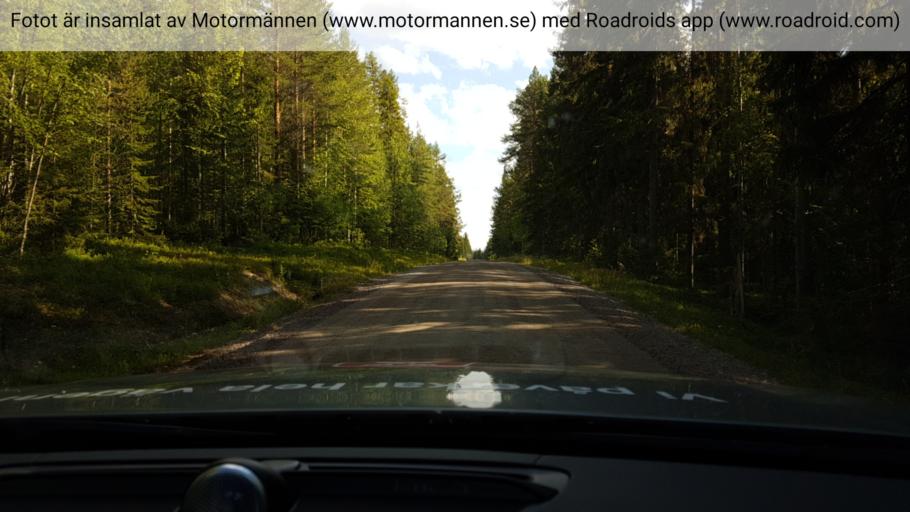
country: SE
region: Vaesterbotten
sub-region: Dorotea Kommun
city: Dorotea
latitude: 63.9574
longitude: 16.0765
